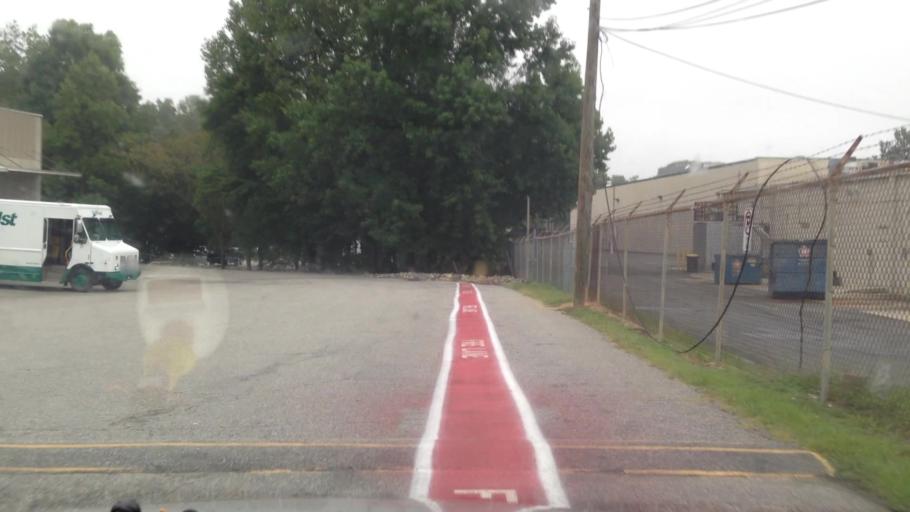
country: US
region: North Carolina
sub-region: Forsyth County
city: Kernersville
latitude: 36.1283
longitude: -80.0692
